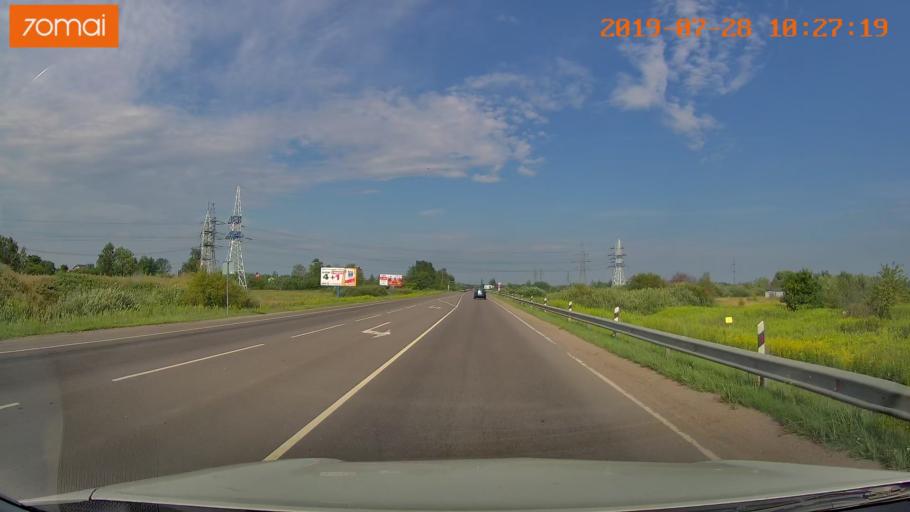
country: RU
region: Kaliningrad
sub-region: Gorod Kaliningrad
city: Kaliningrad
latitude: 54.7703
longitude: 20.5197
